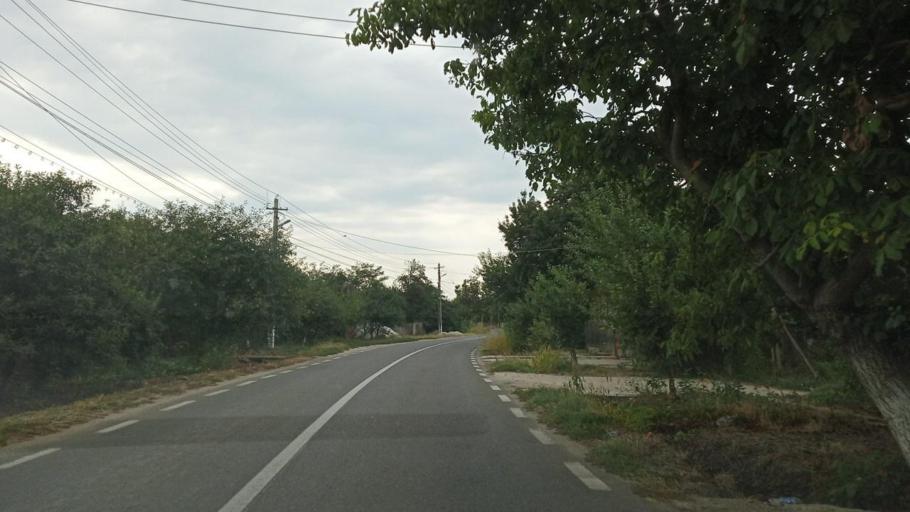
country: RO
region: Giurgiu
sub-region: Comuna Izvoarele
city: Isvoarele
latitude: 44.1706
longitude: 26.3269
